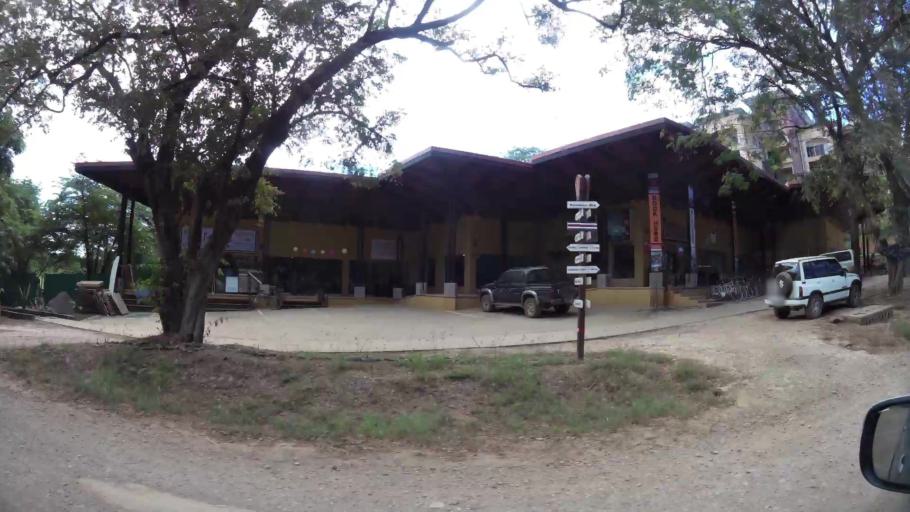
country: CR
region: Guanacaste
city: Santa Cruz
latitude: 10.2915
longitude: -85.8501
